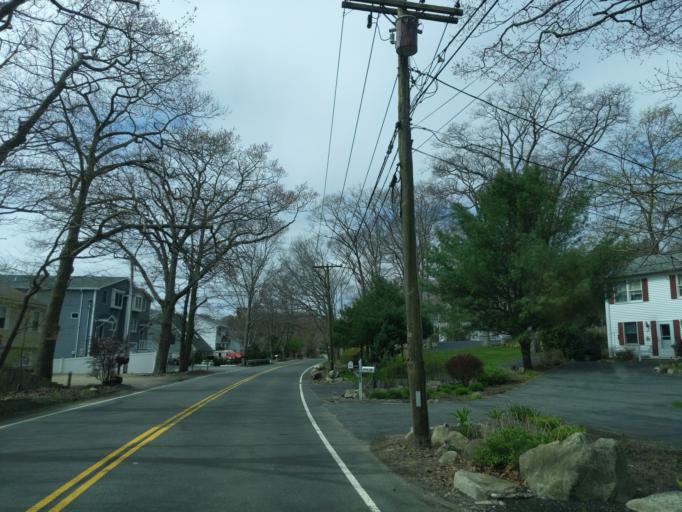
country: US
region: Massachusetts
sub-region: Essex County
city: Rockport
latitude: 42.6274
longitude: -70.6228
